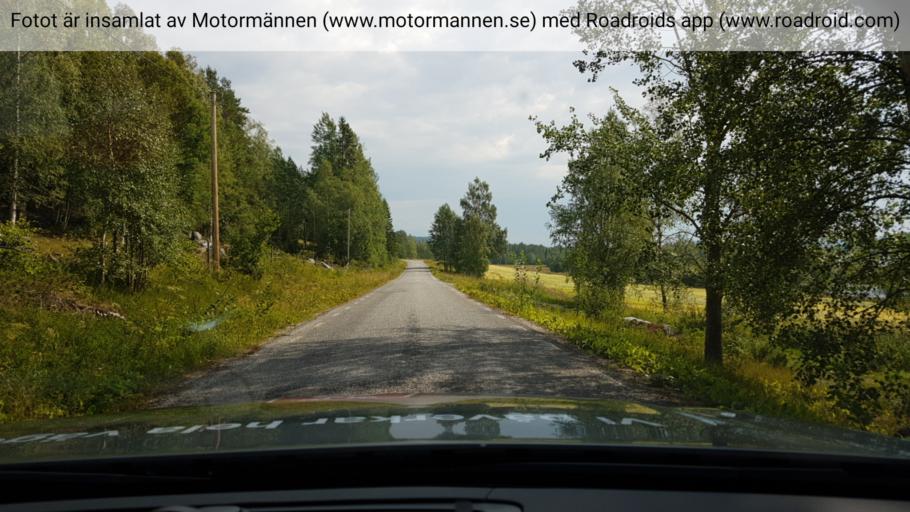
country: SE
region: Jaemtland
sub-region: OEstersunds Kommun
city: Brunflo
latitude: 63.0060
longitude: 15.1118
